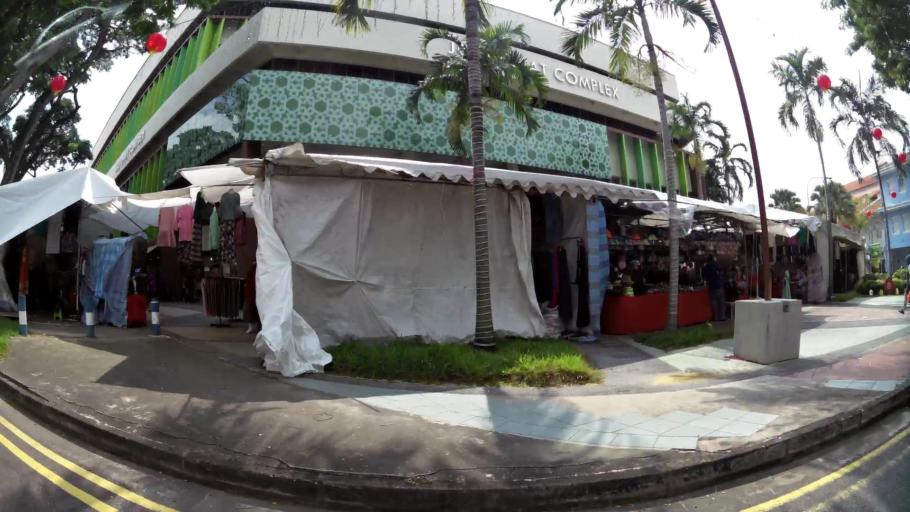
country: SG
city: Singapore
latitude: 1.3161
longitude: 103.8980
